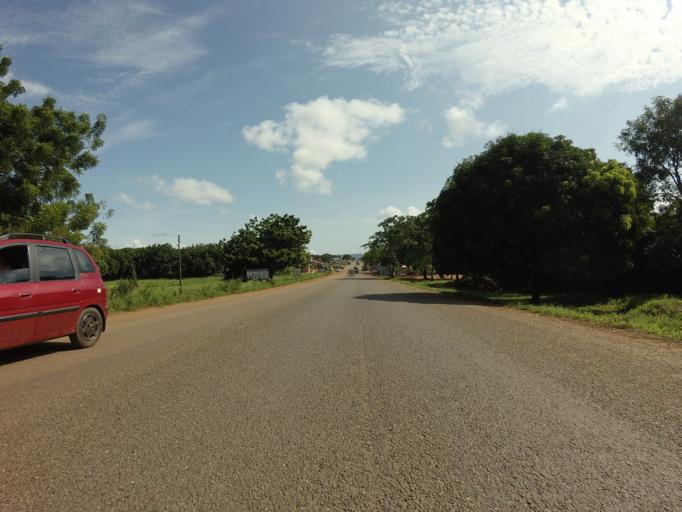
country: GH
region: Eastern
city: Aburi
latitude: 5.8025
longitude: -0.1260
